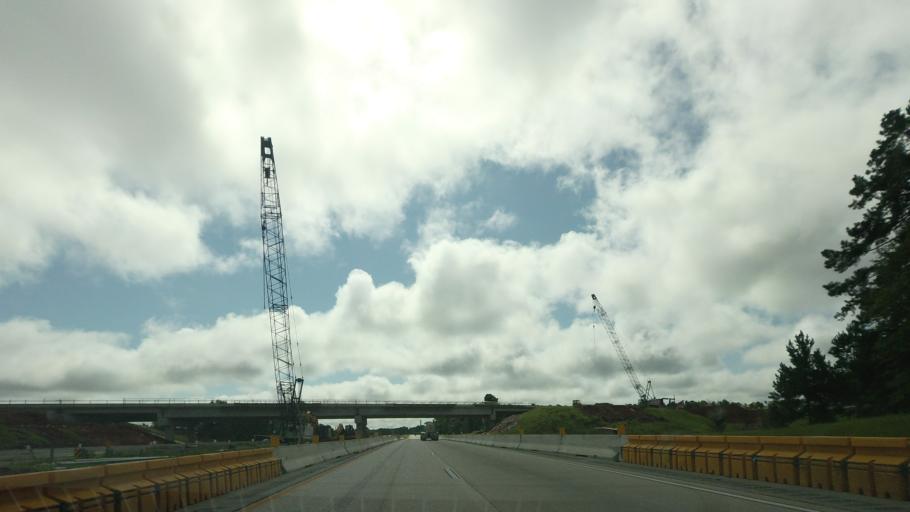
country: US
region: Georgia
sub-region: Twiggs County
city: Jeffersonville
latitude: 32.6240
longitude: -83.3708
